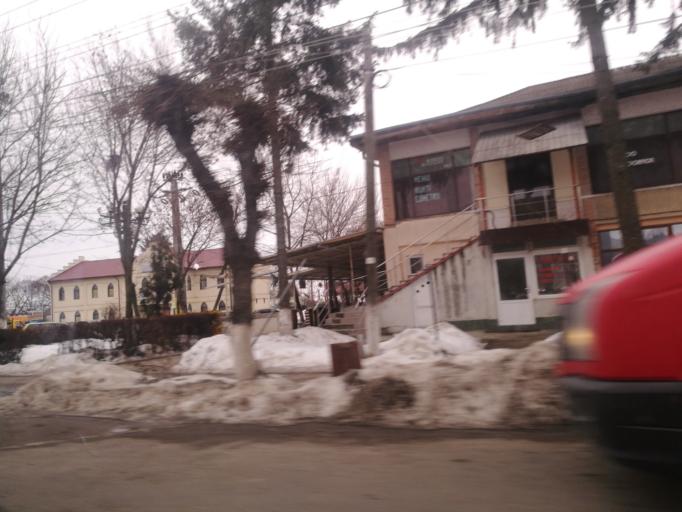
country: RO
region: Iasi
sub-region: Comuna Ruginoasa
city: Ruginoasa
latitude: 47.2425
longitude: 26.8442
